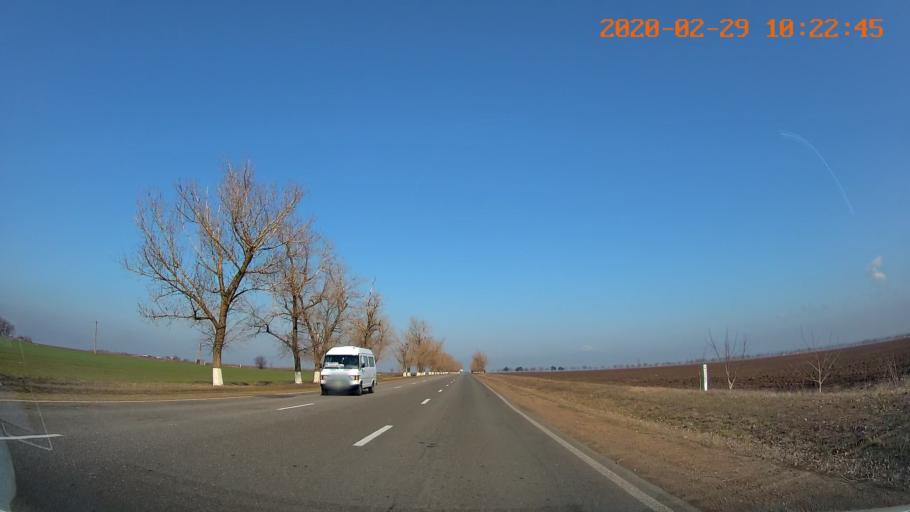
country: MD
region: Telenesti
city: Tiraspolul Nou
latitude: 46.8789
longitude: 29.6055
